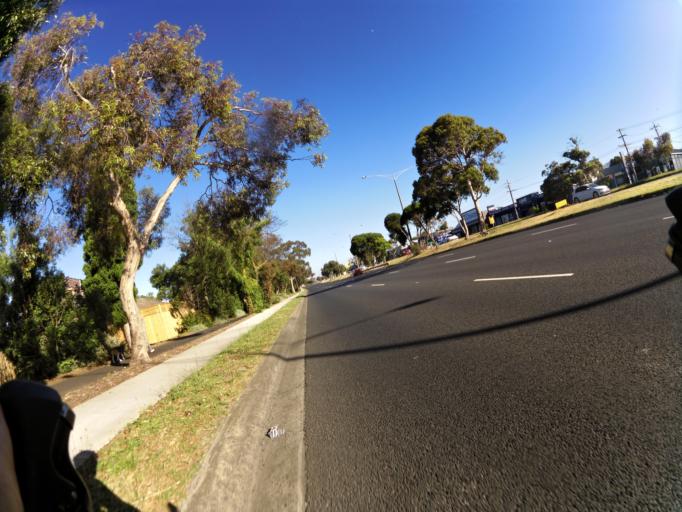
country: AU
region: Victoria
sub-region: Bayside
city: Moorabbin
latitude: -37.9304
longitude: 145.0317
